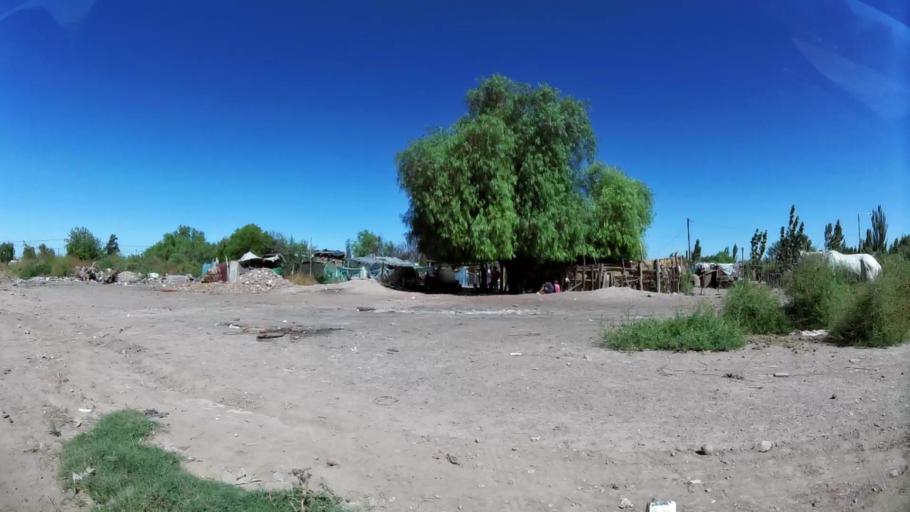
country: AR
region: Mendoza
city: Las Heras
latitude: -32.8222
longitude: -68.8259
